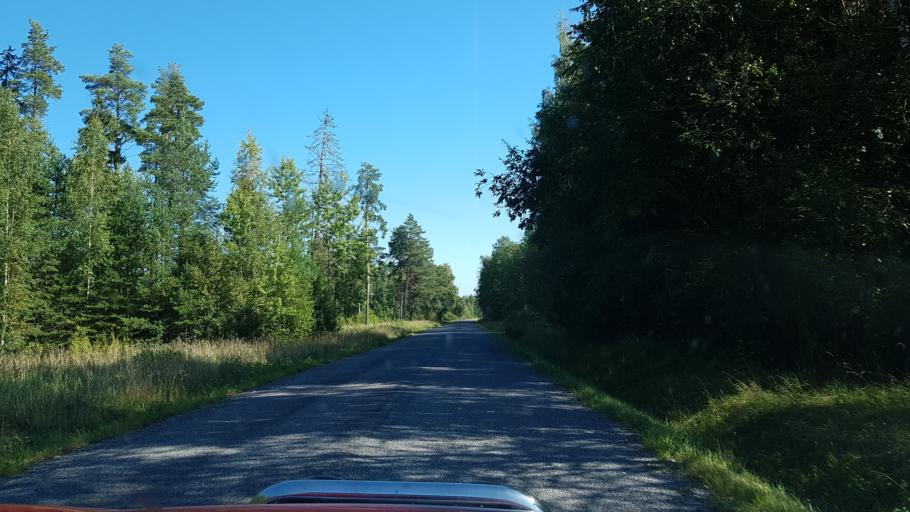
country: EE
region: Polvamaa
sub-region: Polva linn
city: Polva
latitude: 58.2101
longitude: 27.0864
